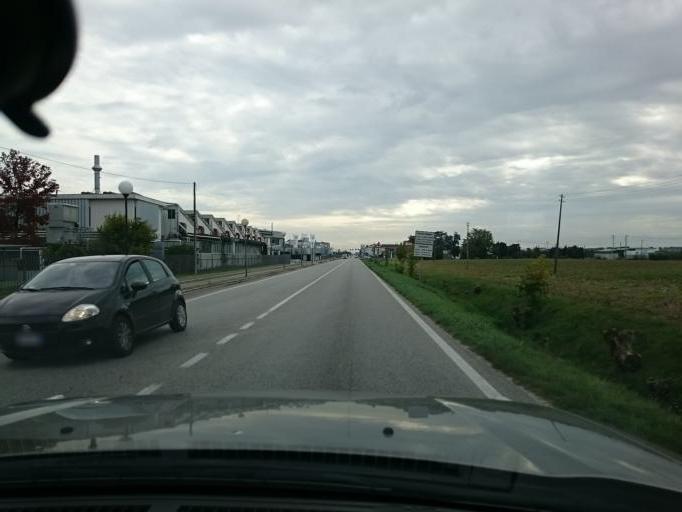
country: IT
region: Veneto
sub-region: Provincia di Padova
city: Sant'Angelo di Piove di Sacco
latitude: 45.3193
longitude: 12.0023
